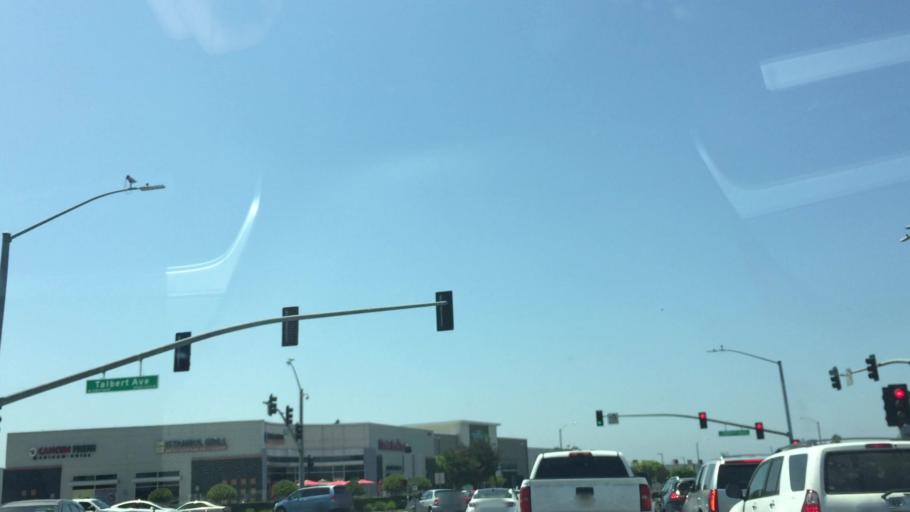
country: US
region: California
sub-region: Orange County
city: Fountain Valley
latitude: 33.7024
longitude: -117.9346
